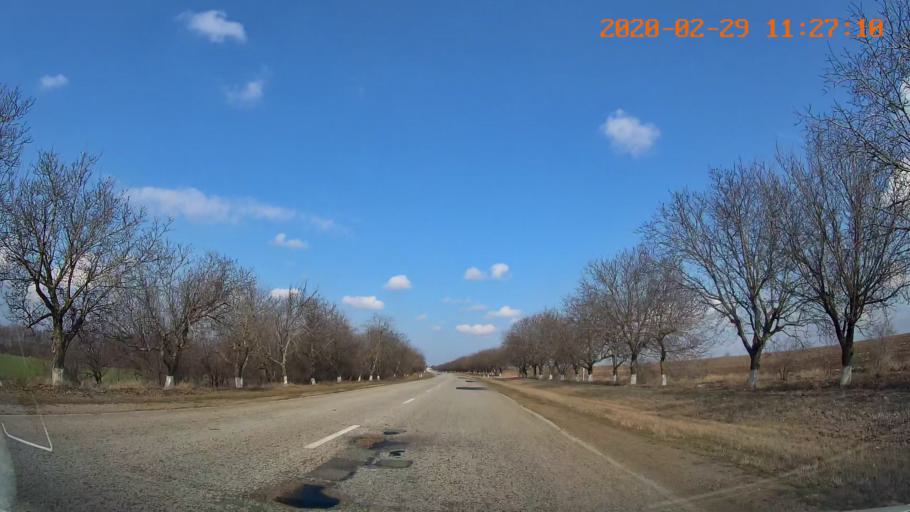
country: MD
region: Telenesti
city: Cocieri
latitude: 47.4641
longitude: 29.1435
